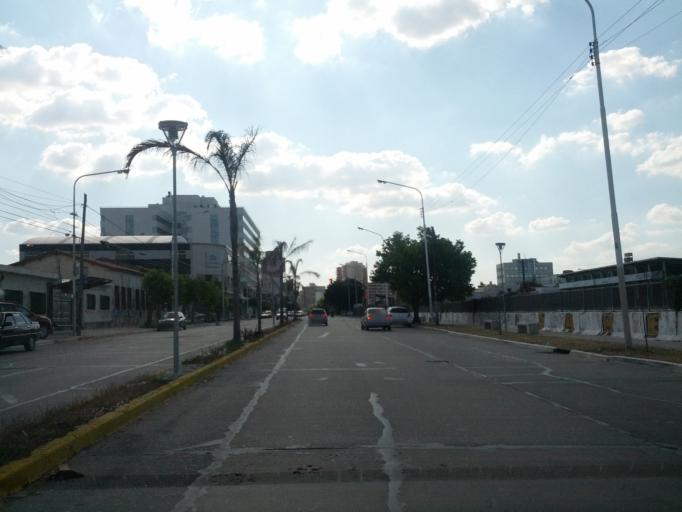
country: AR
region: Buenos Aires
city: San Justo
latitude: -34.6400
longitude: -58.5514
